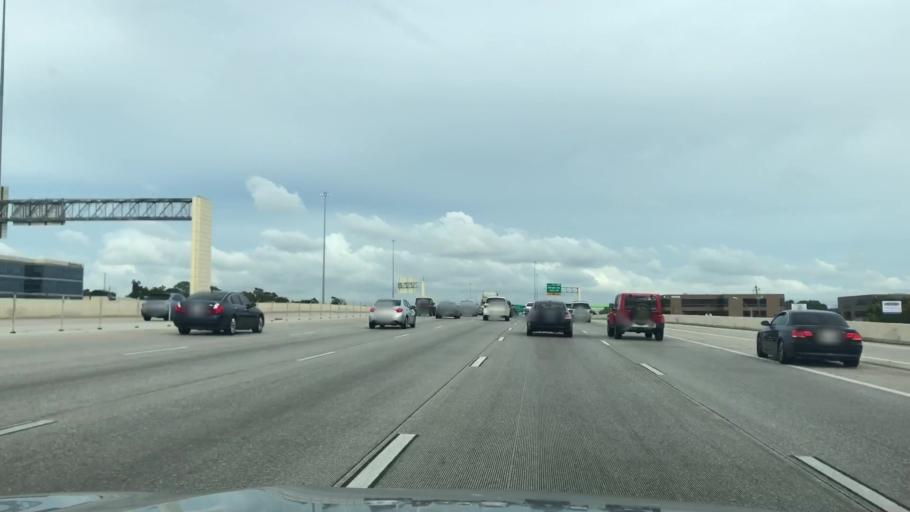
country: US
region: Texas
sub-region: Harris County
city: Hedwig Village
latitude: 29.7834
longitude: -95.5154
